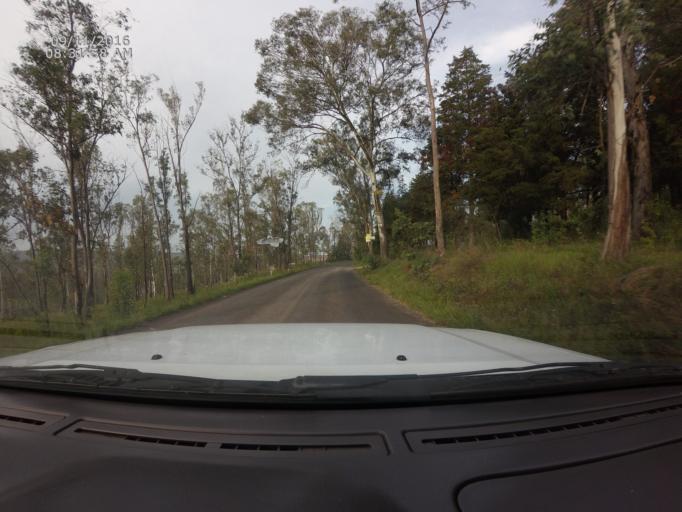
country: MX
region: Michoacan
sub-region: Morelia
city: Morelos
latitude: 19.6303
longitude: -101.2458
